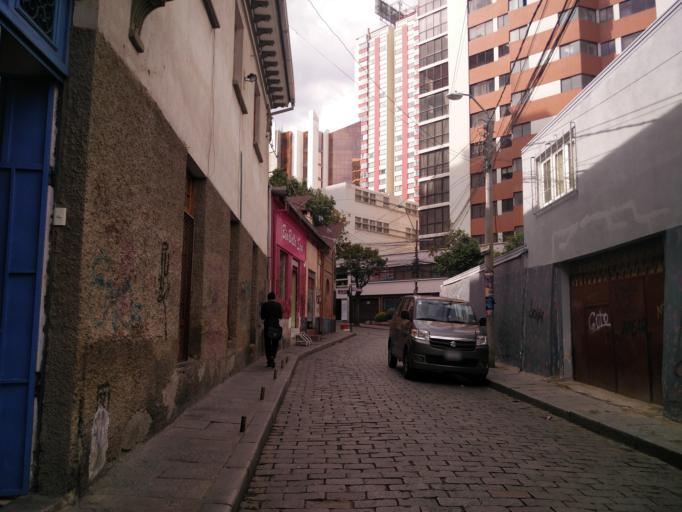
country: BO
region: La Paz
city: La Paz
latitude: -16.5089
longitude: -68.1284
